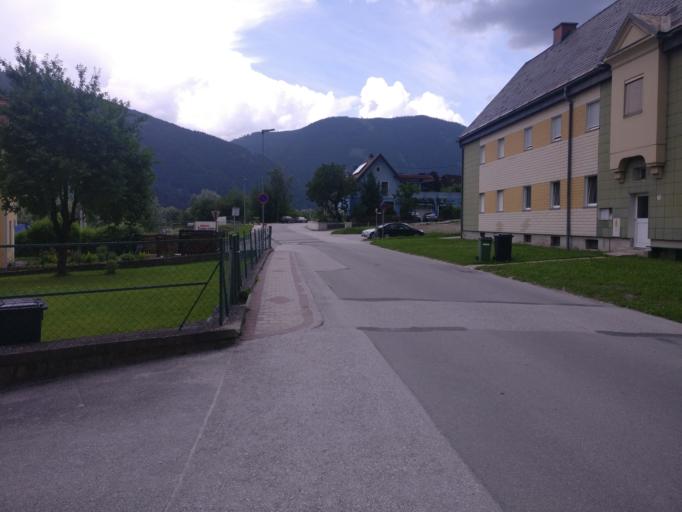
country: AT
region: Styria
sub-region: Politischer Bezirk Liezen
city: Selzthal
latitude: 47.5550
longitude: 14.3224
